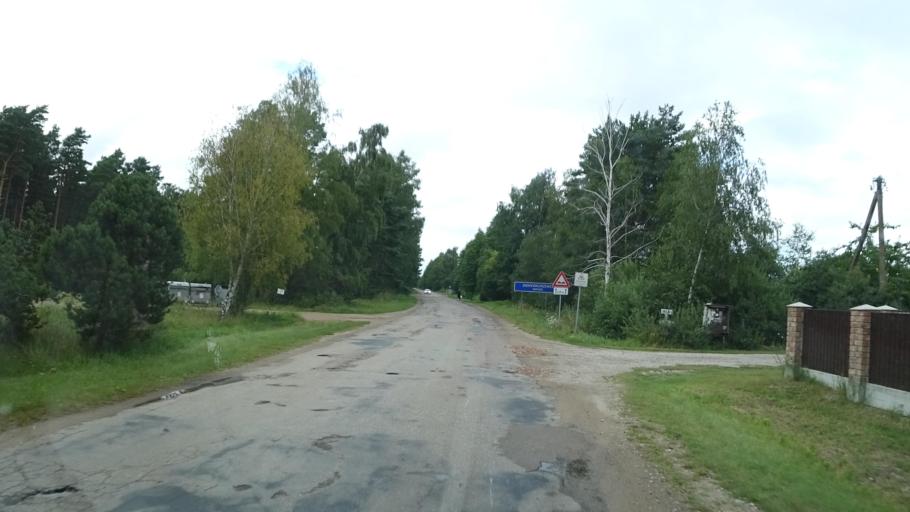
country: LV
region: Liepaja
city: Vec-Liepaja
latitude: 56.6077
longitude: 21.0371
